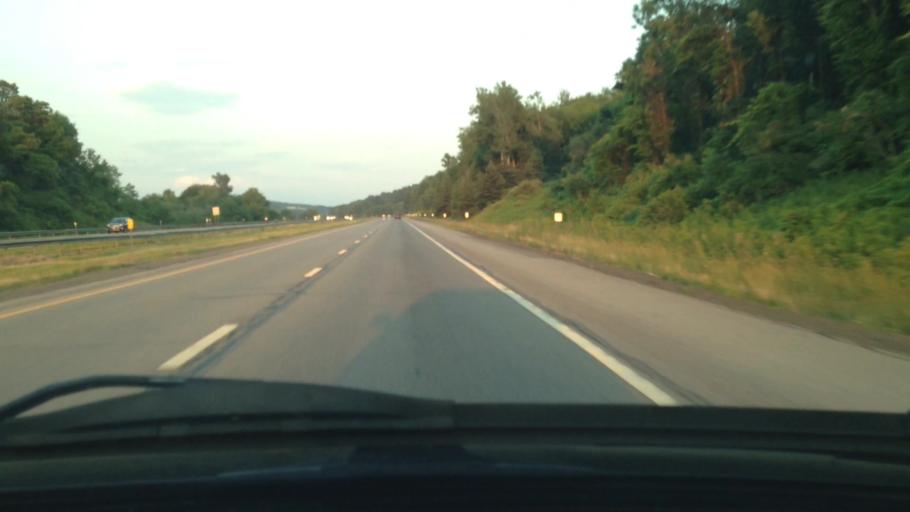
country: US
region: New York
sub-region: Herkimer County
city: Little Falls
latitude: 43.0101
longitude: -74.9135
